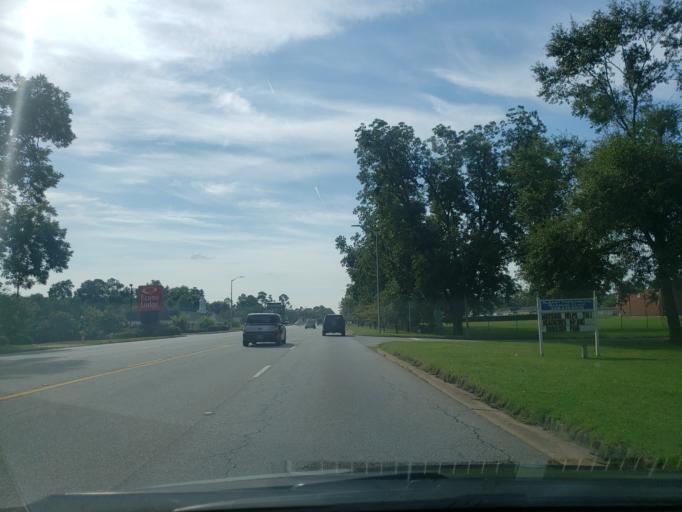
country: US
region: Georgia
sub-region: Dougherty County
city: Albany
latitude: 31.5896
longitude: -84.1890
